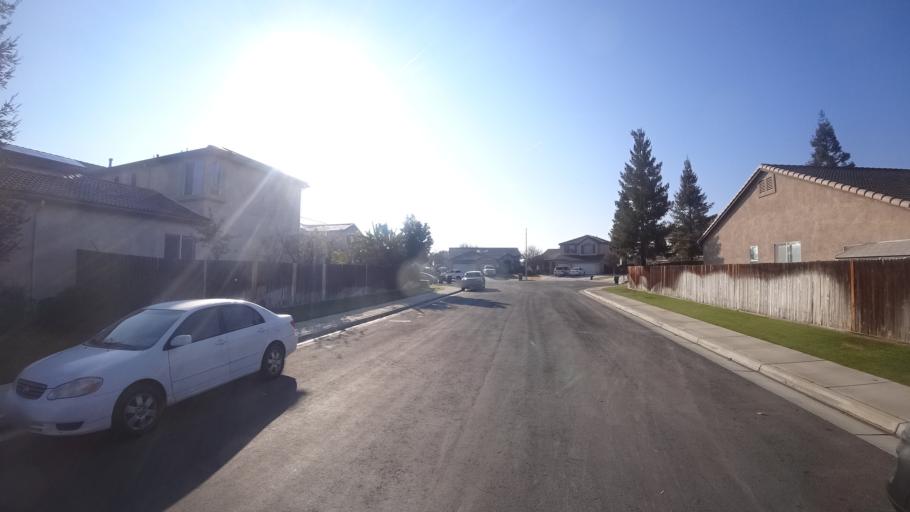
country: US
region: California
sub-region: Kern County
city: Greenacres
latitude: 35.3093
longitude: -119.1216
